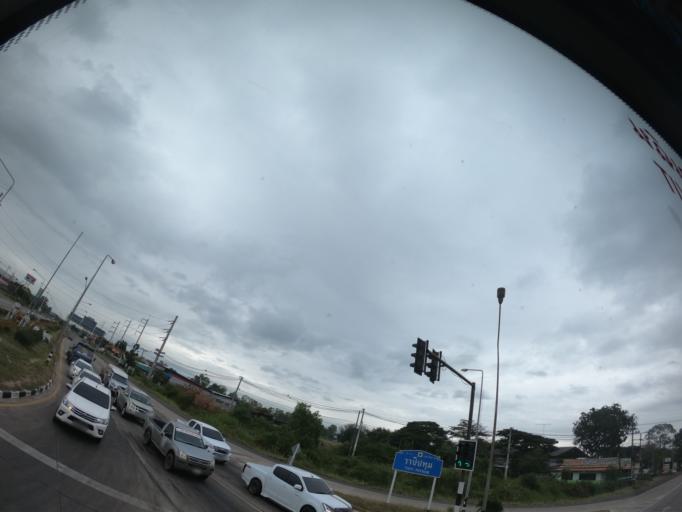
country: TH
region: Roi Et
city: Roi Et
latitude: 16.0429
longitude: 103.6318
